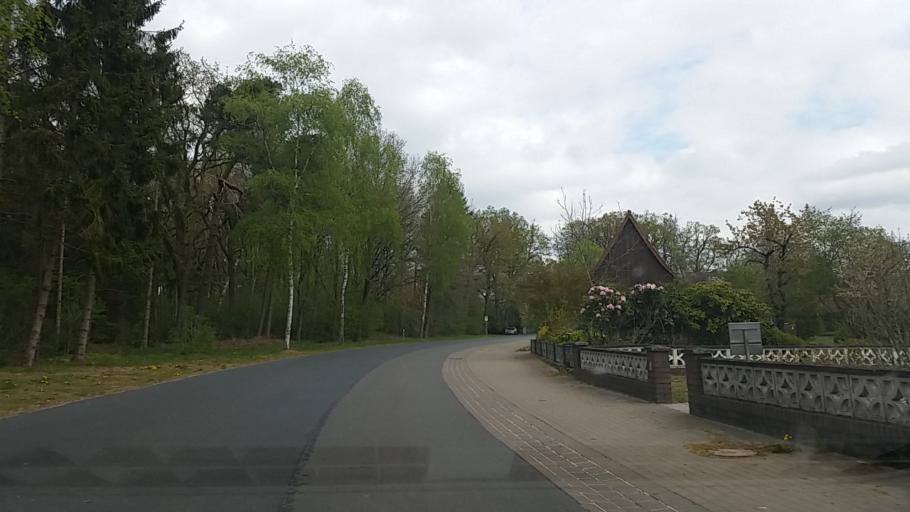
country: DE
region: Lower Saxony
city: Otter
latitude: 53.1846
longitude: 9.7386
